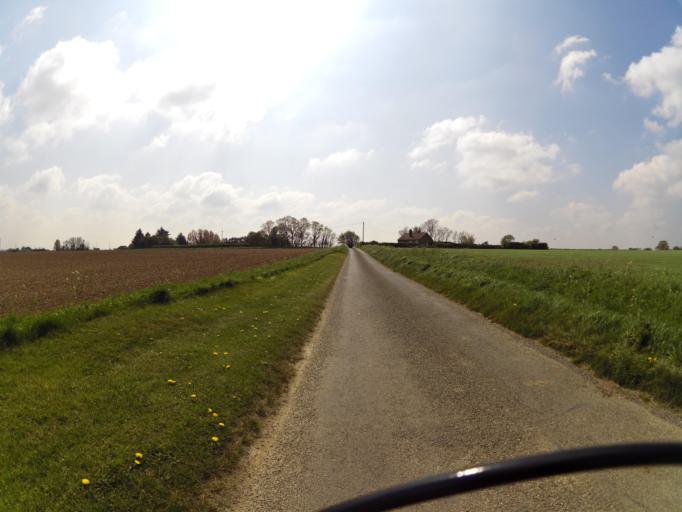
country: GB
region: England
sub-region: Suffolk
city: Bramford
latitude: 52.0766
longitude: 1.0261
